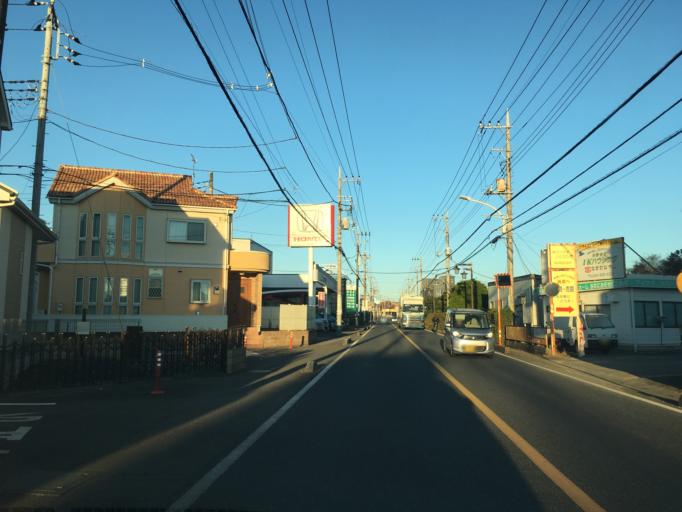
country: JP
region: Saitama
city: Tokorozawa
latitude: 35.8123
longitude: 139.4276
